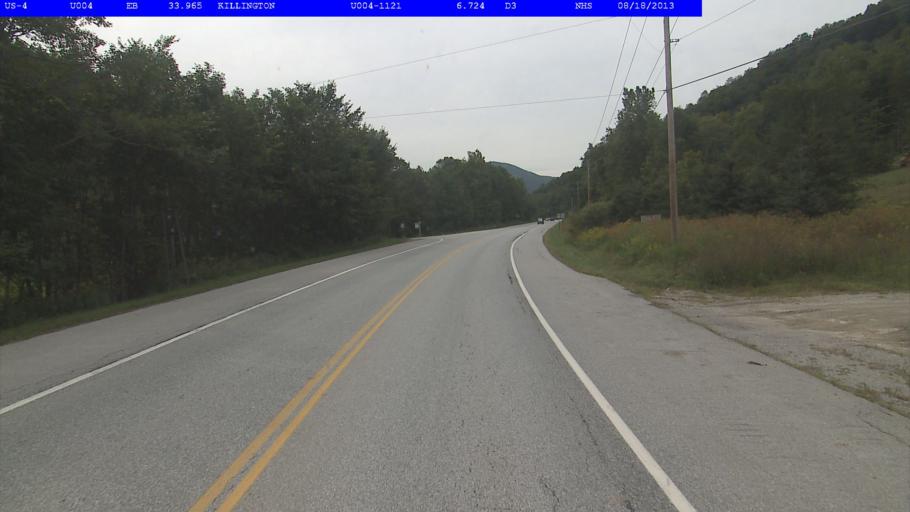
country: US
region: Vermont
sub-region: Rutland County
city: Rutland
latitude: 43.6239
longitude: -72.7607
